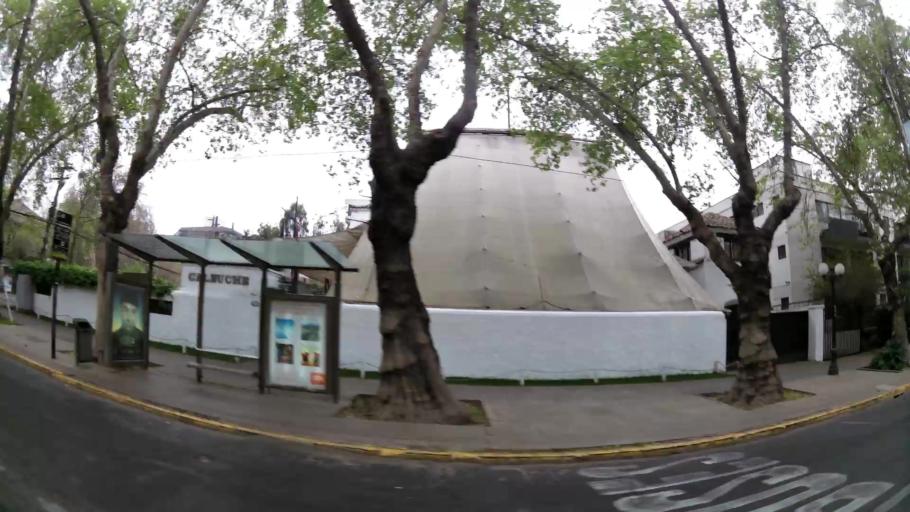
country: CL
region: Santiago Metropolitan
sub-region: Provincia de Santiago
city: Villa Presidente Frei, Nunoa, Santiago, Chile
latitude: -33.4316
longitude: -70.6093
